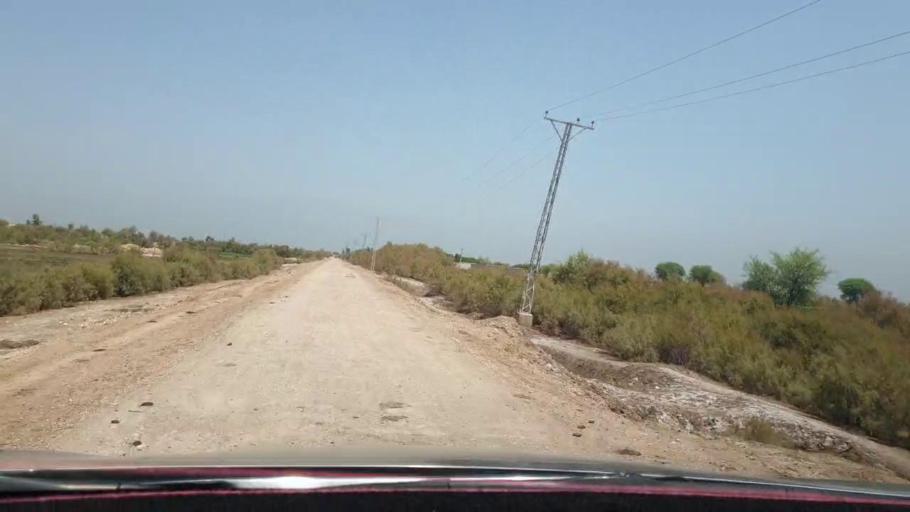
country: PK
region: Sindh
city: Warah
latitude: 27.4059
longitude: 67.6936
